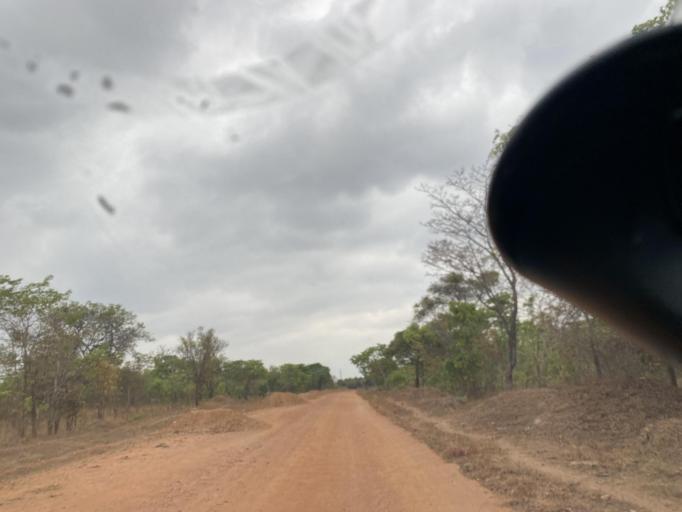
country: ZM
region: Lusaka
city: Chongwe
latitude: -15.2247
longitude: 28.7432
